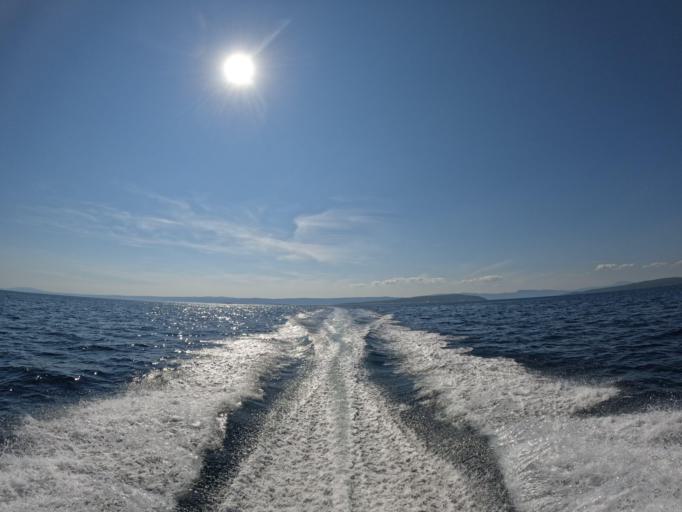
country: HR
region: Primorsko-Goranska
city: Punat
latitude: 44.9569
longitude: 14.6139
